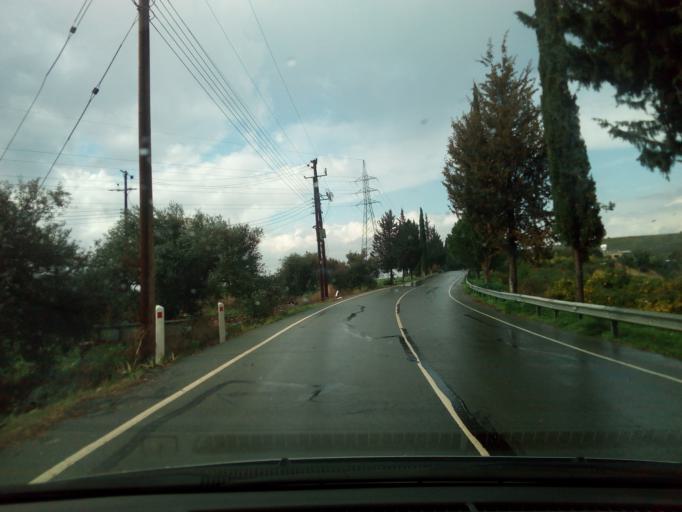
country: CY
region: Pafos
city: Polis
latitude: 35.0211
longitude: 32.4455
